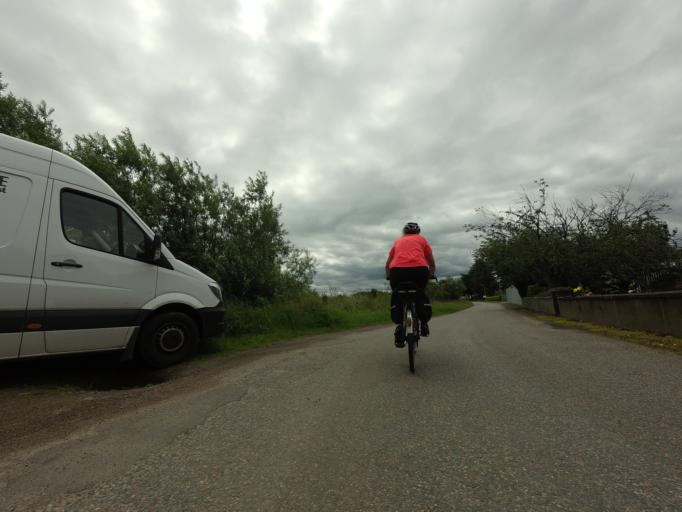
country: GB
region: Scotland
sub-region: Moray
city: Forres
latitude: 57.6148
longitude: -3.6187
